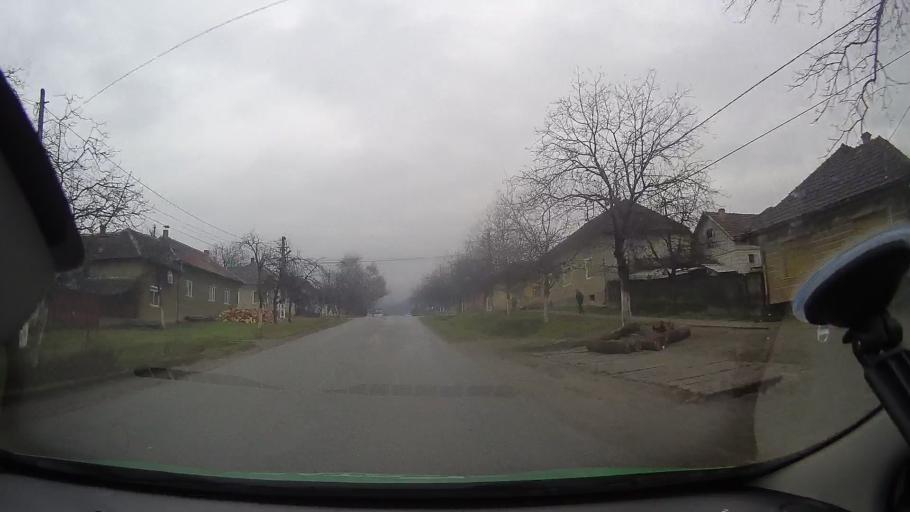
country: RO
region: Arad
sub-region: Comuna Gurahont
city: Gurahont
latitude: 46.2720
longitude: 22.3392
